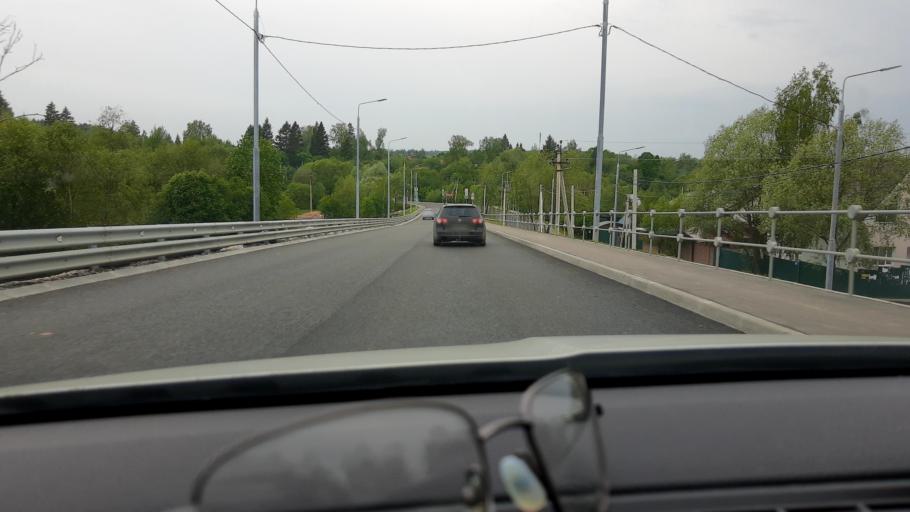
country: RU
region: Moskovskaya
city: Vatutinki
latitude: 55.5166
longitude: 37.3317
